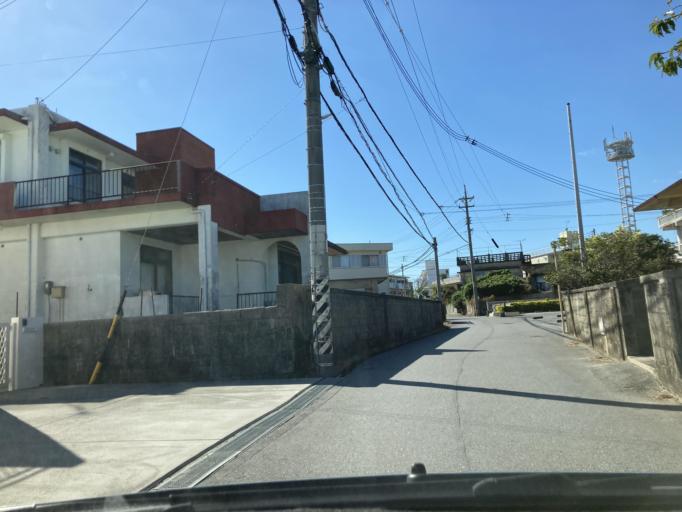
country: JP
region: Okinawa
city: Okinawa
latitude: 26.3632
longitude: 127.8257
